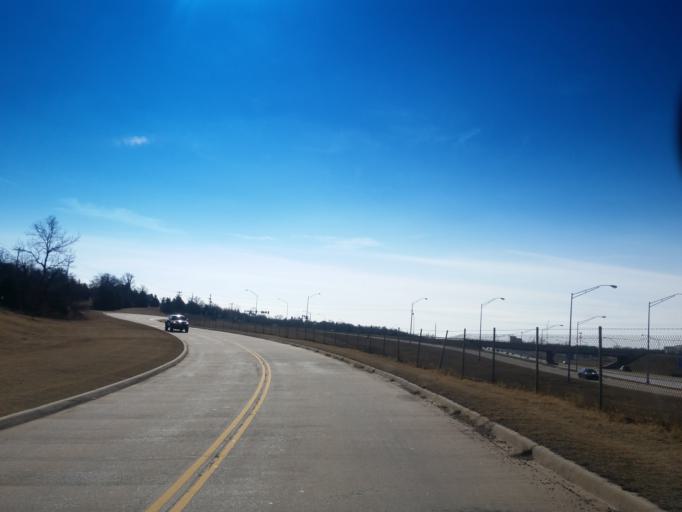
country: US
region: Oklahoma
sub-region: Oklahoma County
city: Edmond
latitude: 35.6414
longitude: -97.4243
